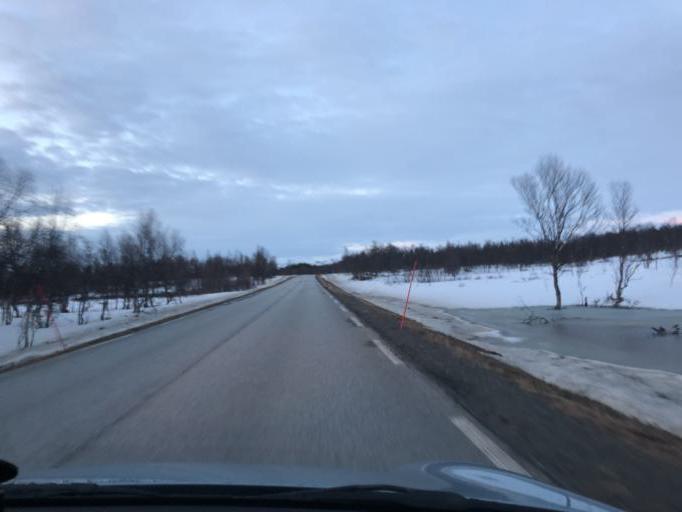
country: NO
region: Sor-Trondelag
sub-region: Tydal
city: Aas
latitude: 62.7125
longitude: 11.8121
